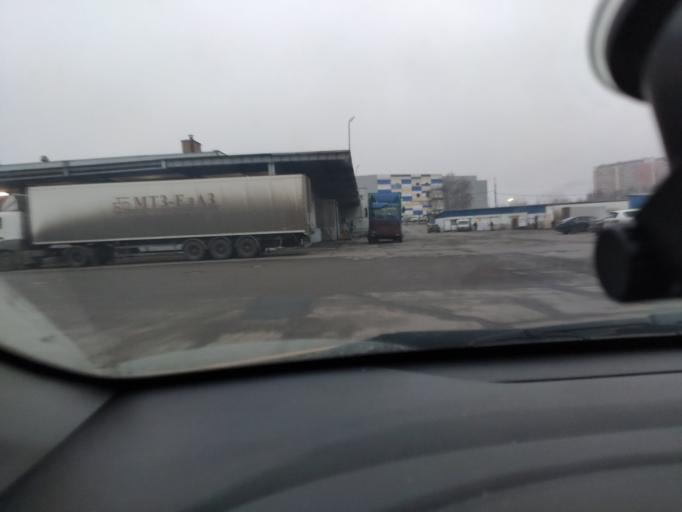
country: RU
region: Moskovskaya
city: Biryulevo Zapadnoye
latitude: 55.5924
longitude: 37.6220
